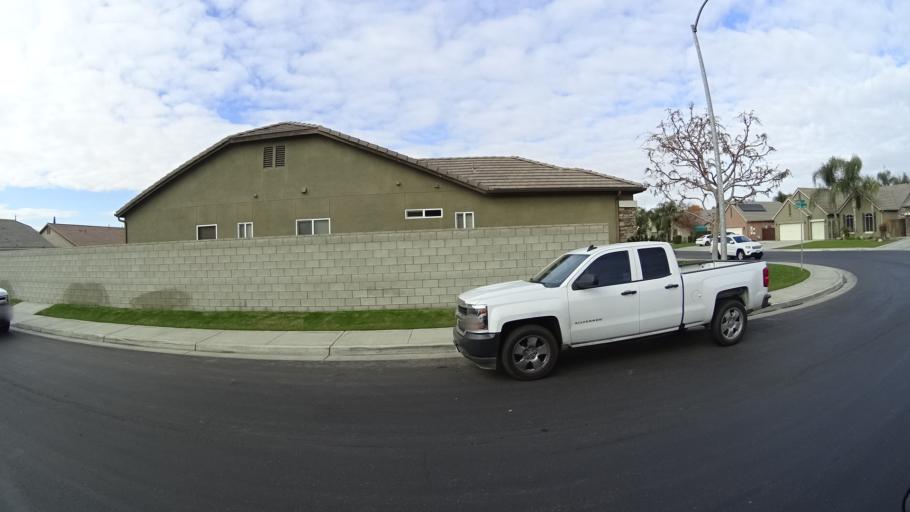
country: US
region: California
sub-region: Kern County
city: Rosedale
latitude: 35.3000
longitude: -119.1290
